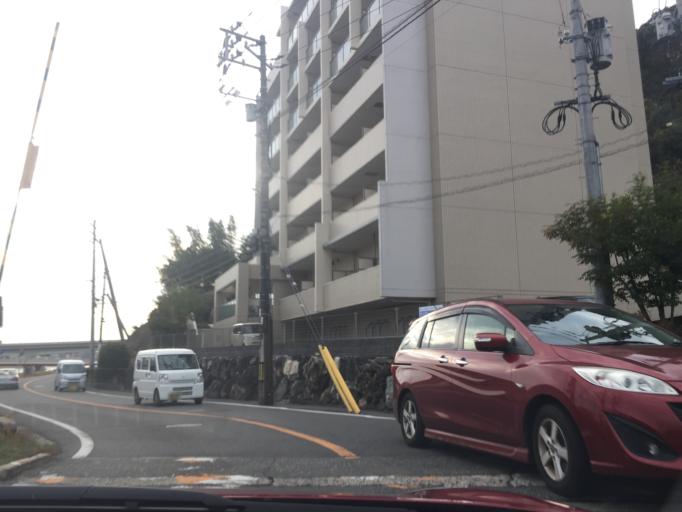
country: JP
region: Hiroshima
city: Hiroshima-shi
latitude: 34.4139
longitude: 132.4453
